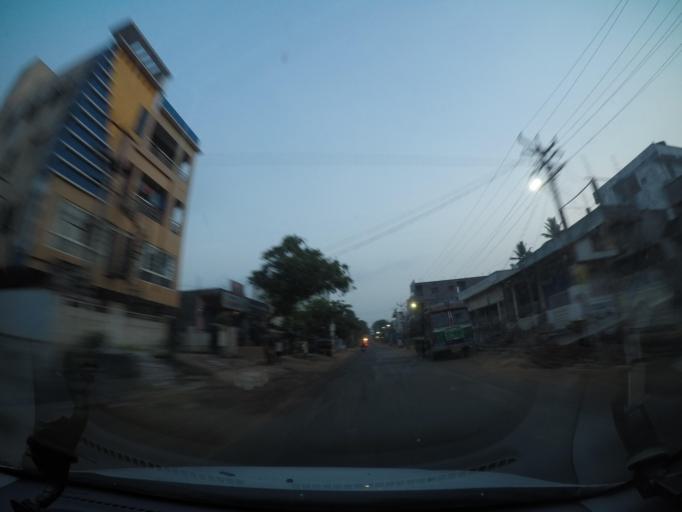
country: IN
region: Andhra Pradesh
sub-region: West Godavari
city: Tadepallegudem
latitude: 16.8175
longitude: 81.4055
